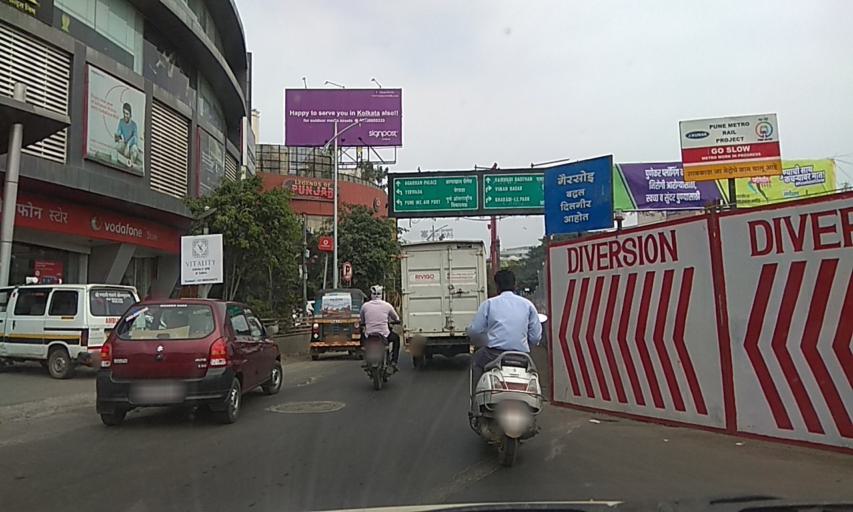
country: IN
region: Maharashtra
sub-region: Pune Division
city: Shivaji Nagar
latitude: 18.5432
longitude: 73.9049
